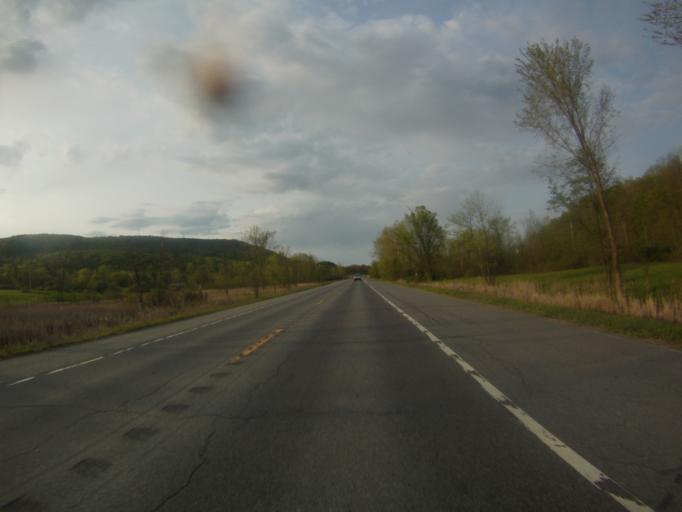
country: US
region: New York
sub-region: Essex County
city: Ticonderoga
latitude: 43.9039
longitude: -73.4265
